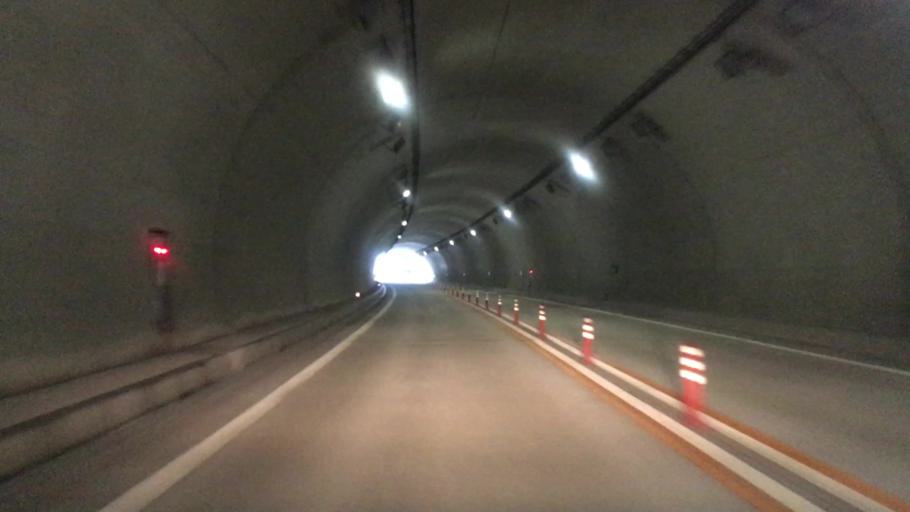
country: JP
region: Tottori
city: Tottori
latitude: 35.5555
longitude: 134.2813
